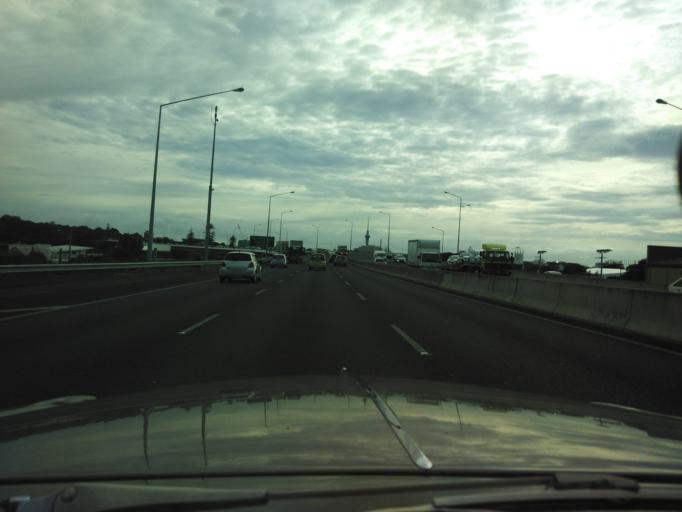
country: NZ
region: Auckland
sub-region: Auckland
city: Auckland
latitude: -36.8768
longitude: 174.7815
